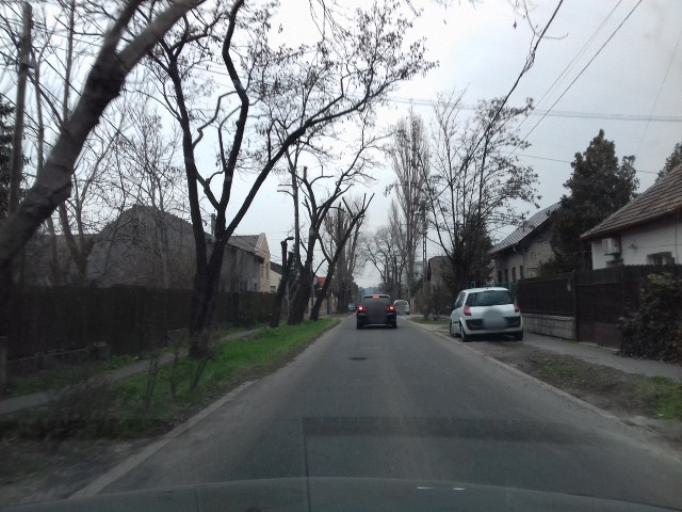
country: HU
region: Budapest
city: Budapest XVI. keruelet
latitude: 47.5300
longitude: 19.1587
